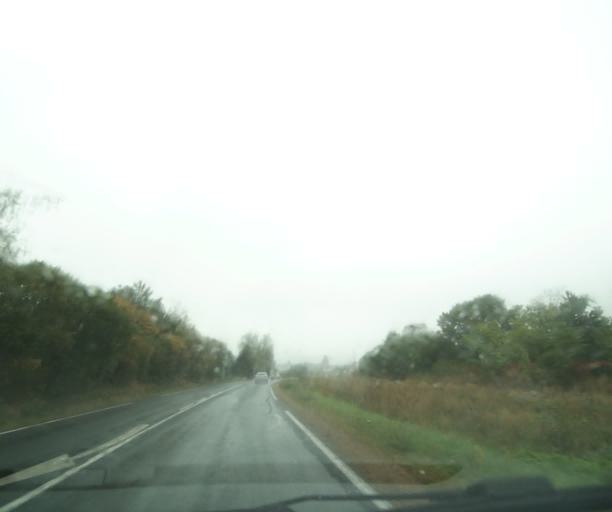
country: FR
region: Auvergne
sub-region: Departement du Puy-de-Dome
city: Blanzat
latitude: 45.8326
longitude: 3.0867
